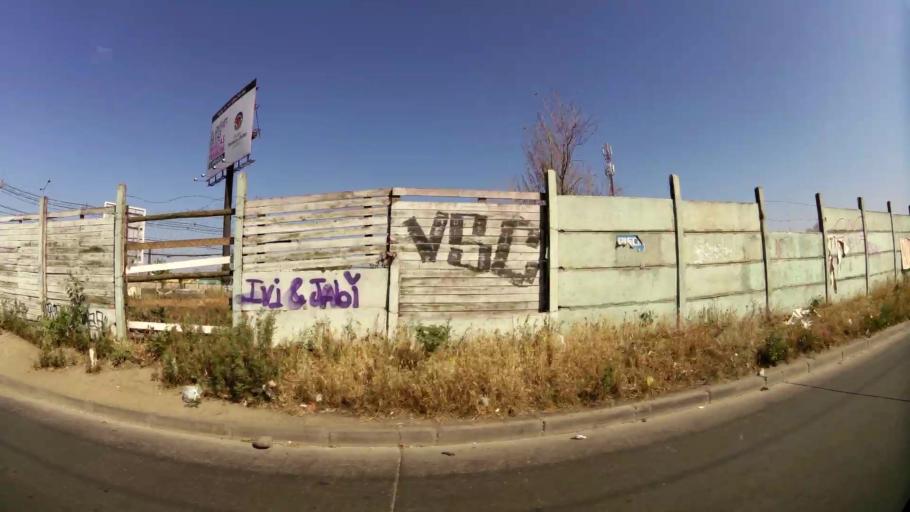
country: CL
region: Santiago Metropolitan
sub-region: Provincia de Chacabuco
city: Chicureo Abajo
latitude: -33.3666
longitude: -70.6810
